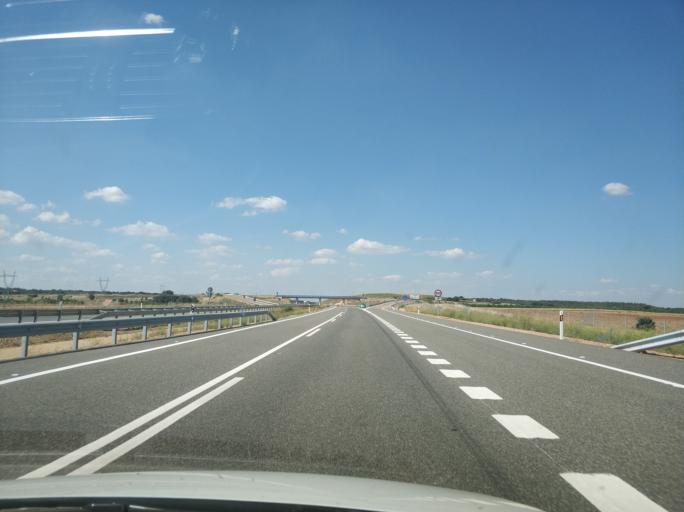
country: ES
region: Castille and Leon
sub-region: Provincia de Zamora
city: Granja de Moreruela
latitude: 41.8254
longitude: -5.7429
